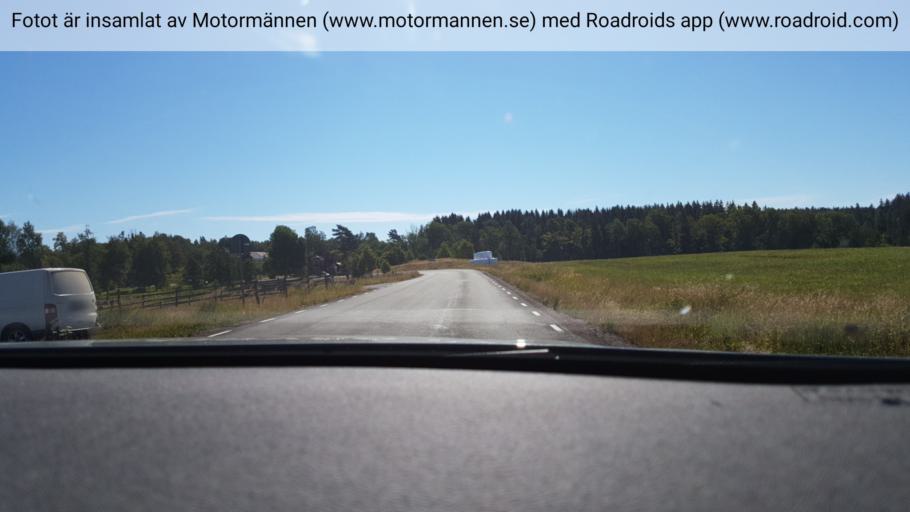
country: SE
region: Vaestra Goetaland
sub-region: Tidaholms Kommun
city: Tidaholm
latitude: 58.1391
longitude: 14.0133
